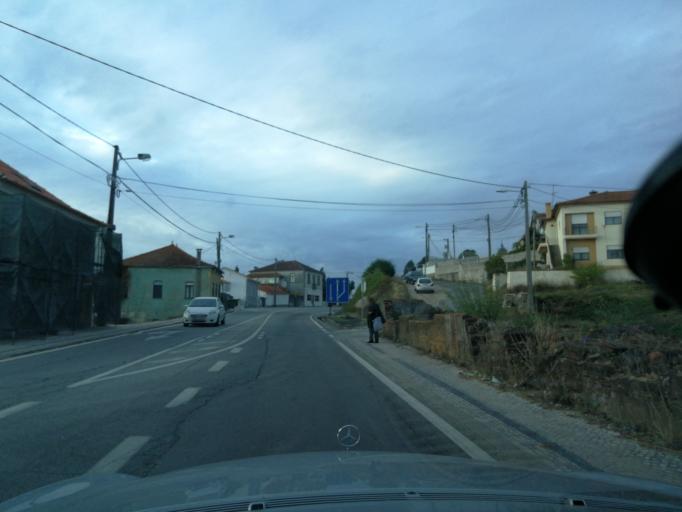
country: PT
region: Aveiro
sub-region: Agueda
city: Agueda
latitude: 40.5783
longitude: -8.4504
